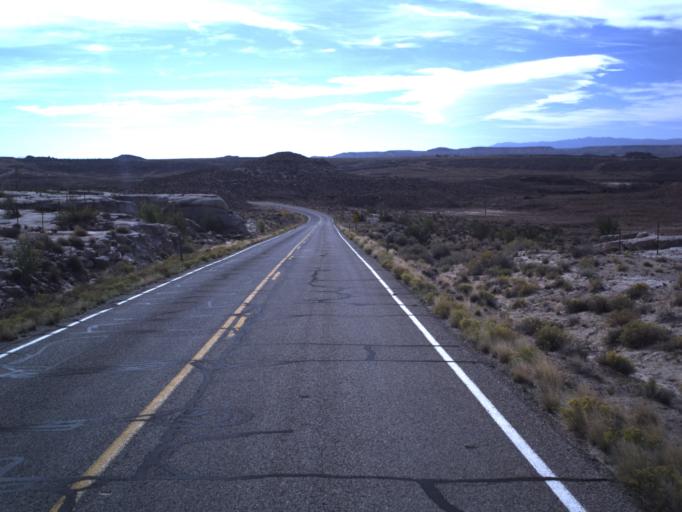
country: US
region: Utah
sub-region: San Juan County
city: Blanding
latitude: 37.3126
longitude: -109.3040
